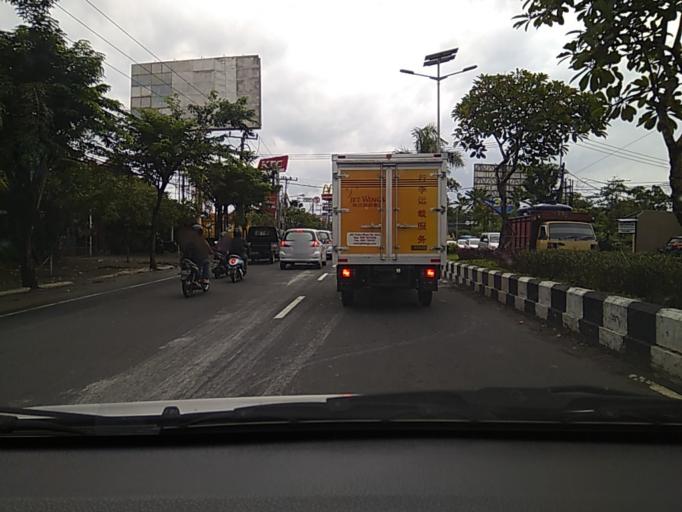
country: ID
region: Bali
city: Jimbaran
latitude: -8.7819
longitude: 115.1797
